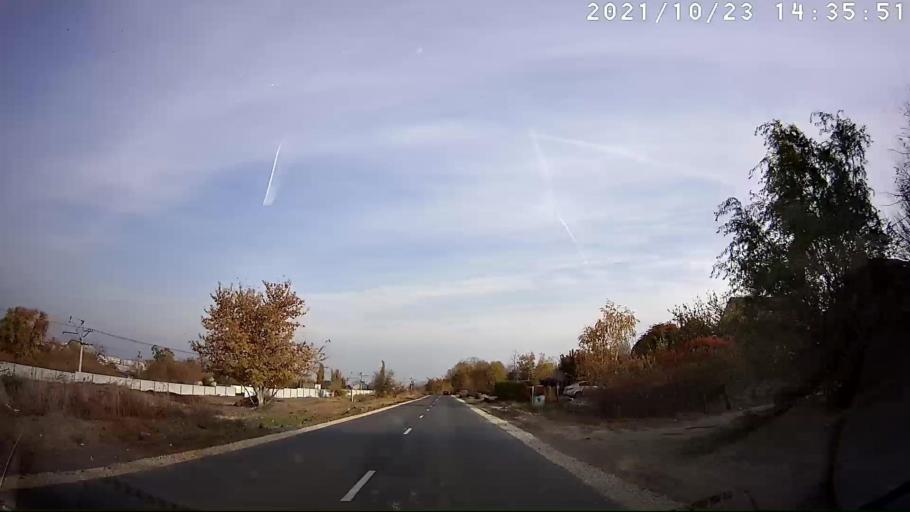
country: RU
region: Volgograd
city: Krasnoslobodsk
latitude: 48.5062
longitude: 44.5357
